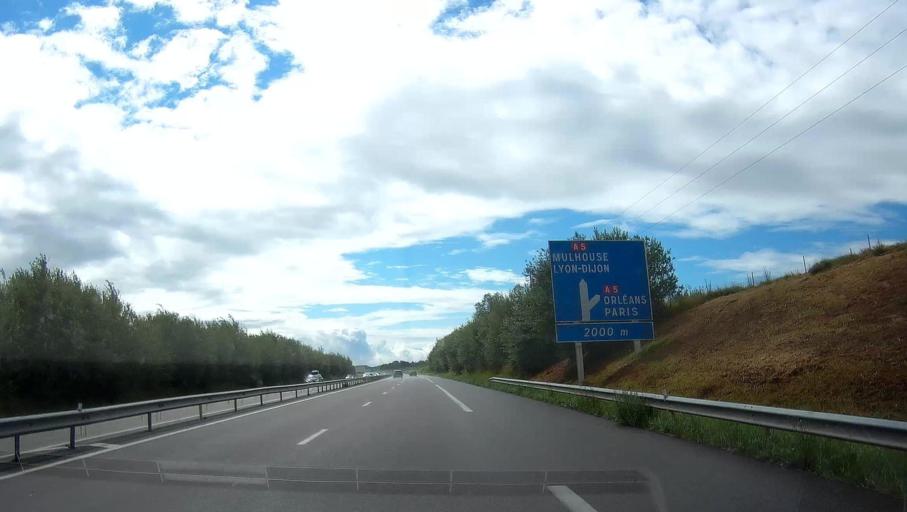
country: FR
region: Champagne-Ardenne
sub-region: Departement de l'Aube
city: Verrieres
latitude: 48.2504
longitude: 4.1677
